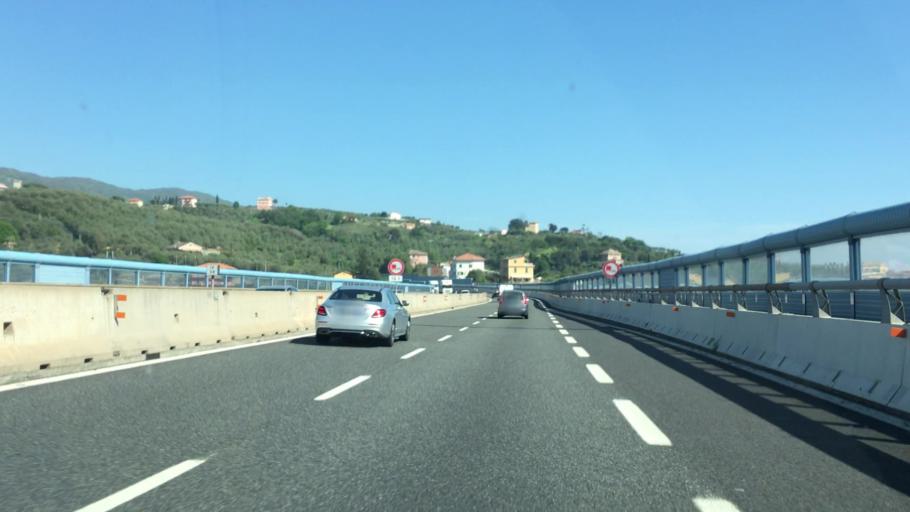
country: IT
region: Liguria
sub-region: Provincia di Genova
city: Chiavari
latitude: 44.3278
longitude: 9.3192
